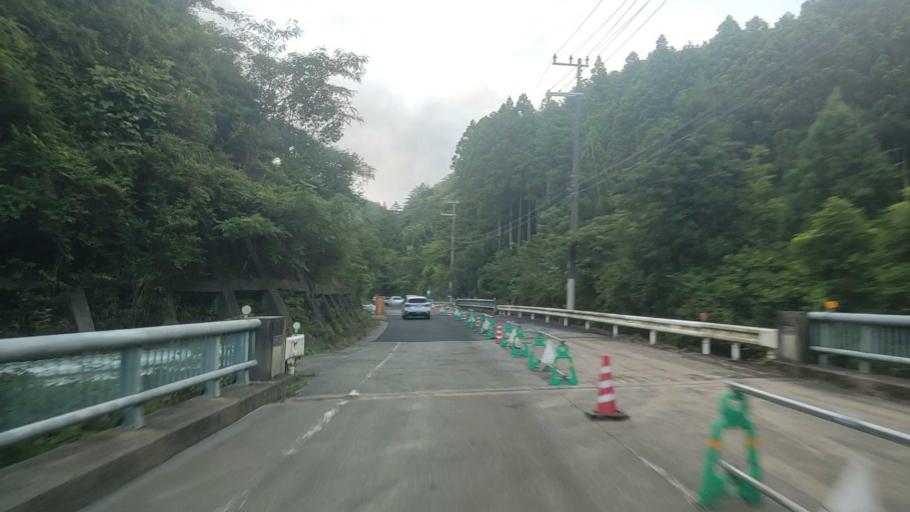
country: JP
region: Wakayama
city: Tanabe
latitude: 33.8311
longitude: 135.6509
